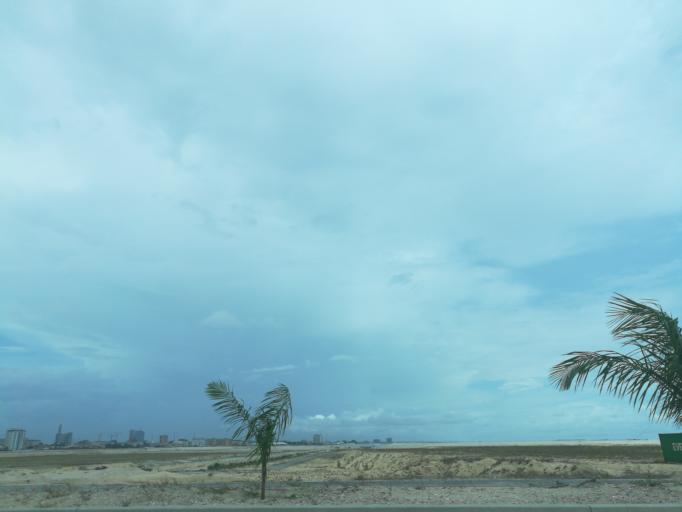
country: NG
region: Lagos
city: Ikoyi
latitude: 6.4160
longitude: 3.4245
